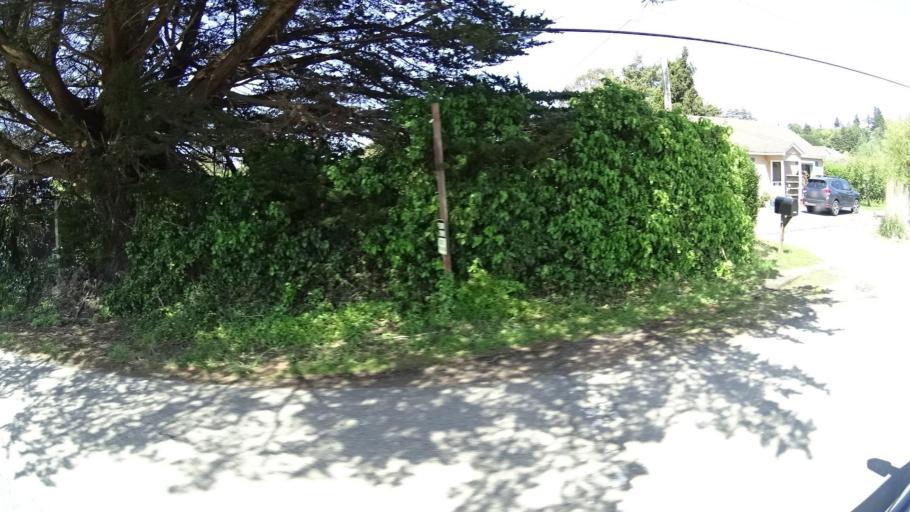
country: US
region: California
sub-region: Humboldt County
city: Fortuna
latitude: 40.5630
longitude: -124.1457
